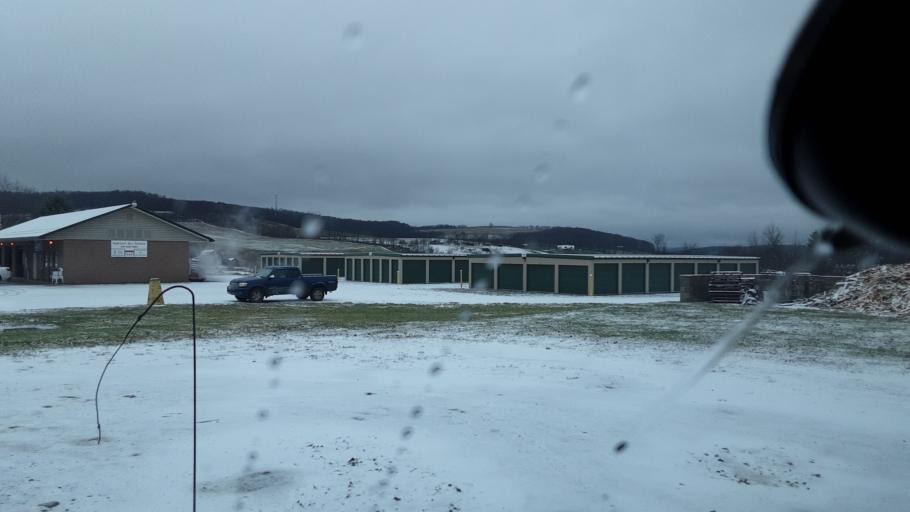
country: US
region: Pennsylvania
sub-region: Potter County
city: Galeton
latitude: 41.9040
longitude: -77.7679
